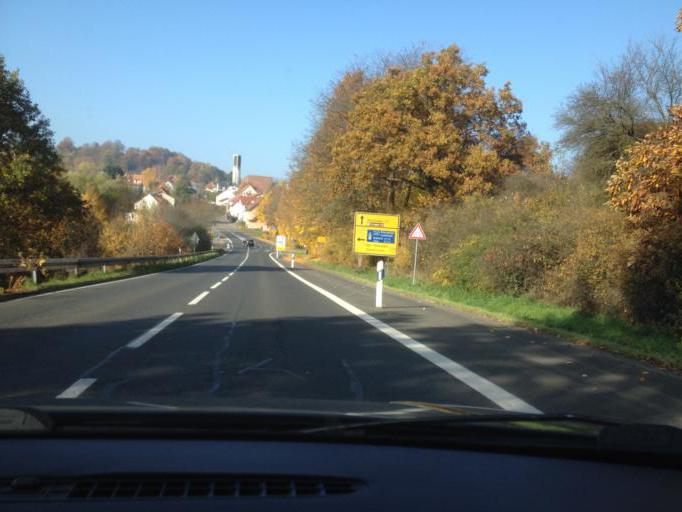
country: DE
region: Saarland
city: Namborn
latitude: 49.5073
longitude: 7.1618
